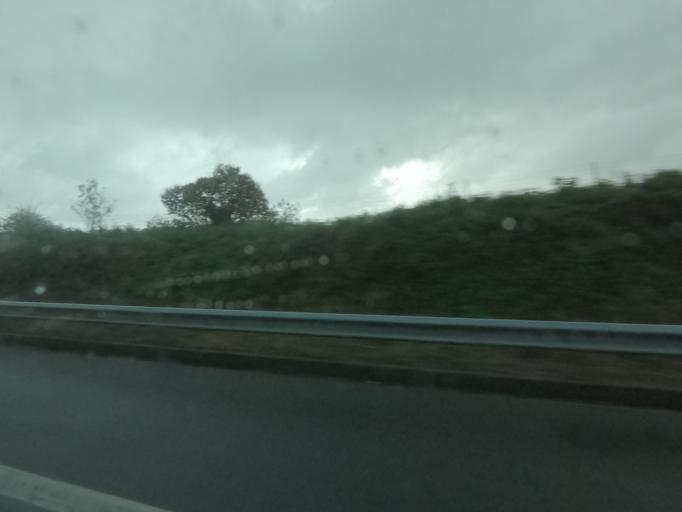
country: ES
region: Galicia
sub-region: Provincia de Pontevedra
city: Marin
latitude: 42.3617
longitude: -8.6402
